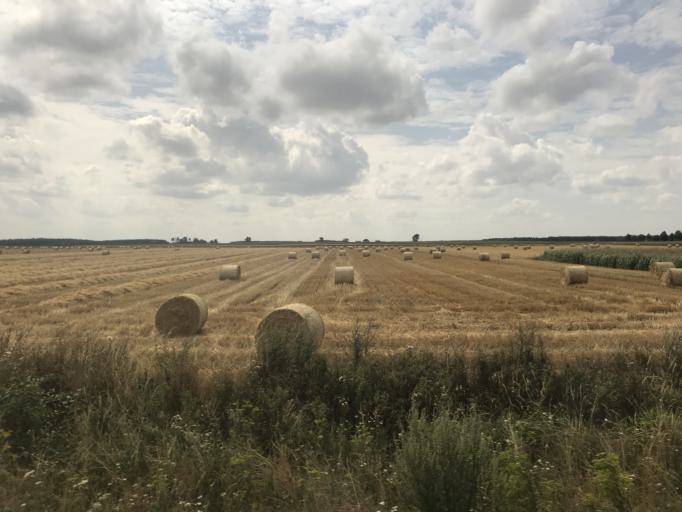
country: PL
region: Greater Poland Voivodeship
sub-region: Powiat gnieznienski
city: Lubowo
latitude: 52.5067
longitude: 17.4911
